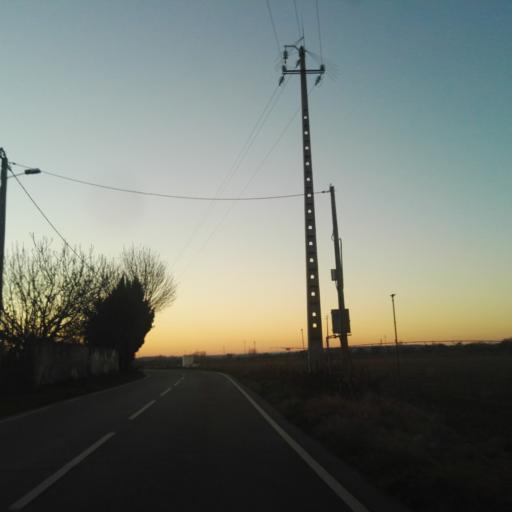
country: PT
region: Santarem
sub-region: Alpiarca
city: Alpiarca
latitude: 39.3029
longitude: -8.5394
